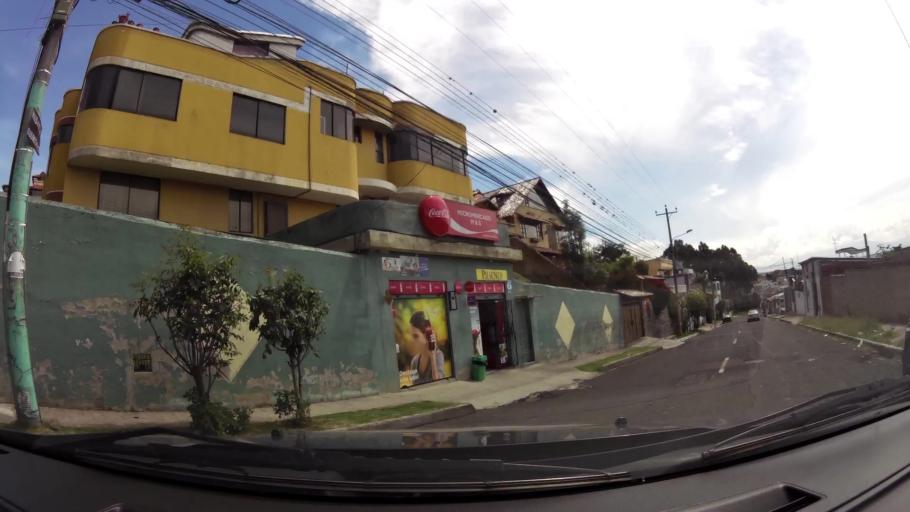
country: EC
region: Pichincha
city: Quito
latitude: -0.2173
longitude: -78.4334
